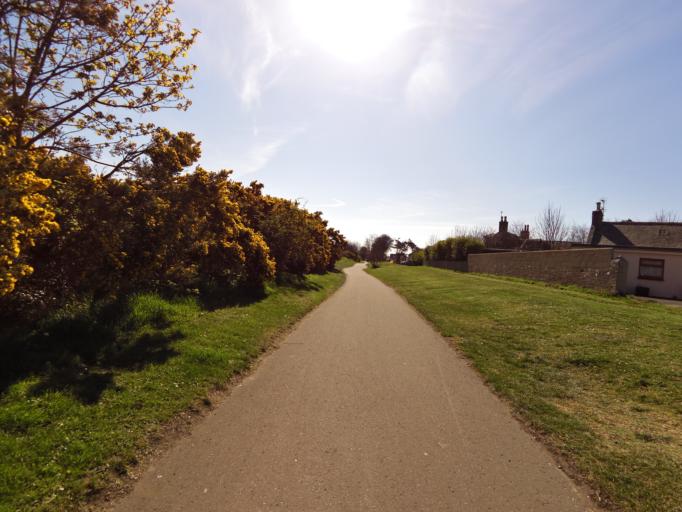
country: GB
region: Scotland
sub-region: Angus
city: Montrose
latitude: 56.7203
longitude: -2.4602
